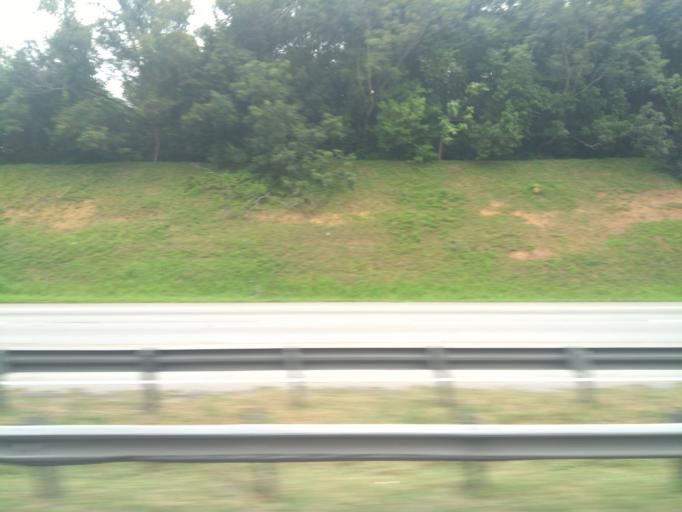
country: MY
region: Melaka
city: Pulau Sebang
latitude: 2.4406
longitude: 102.1992
